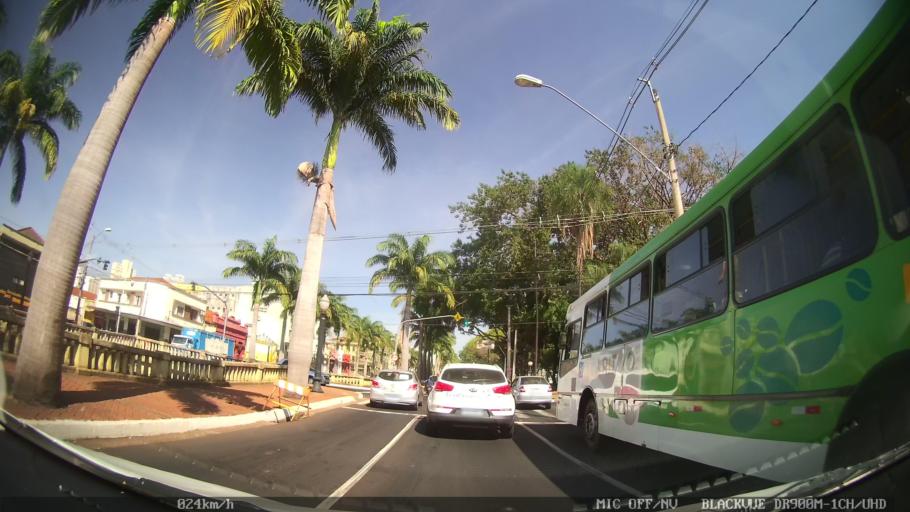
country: BR
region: Sao Paulo
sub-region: Ribeirao Preto
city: Ribeirao Preto
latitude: -21.1714
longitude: -47.8124
